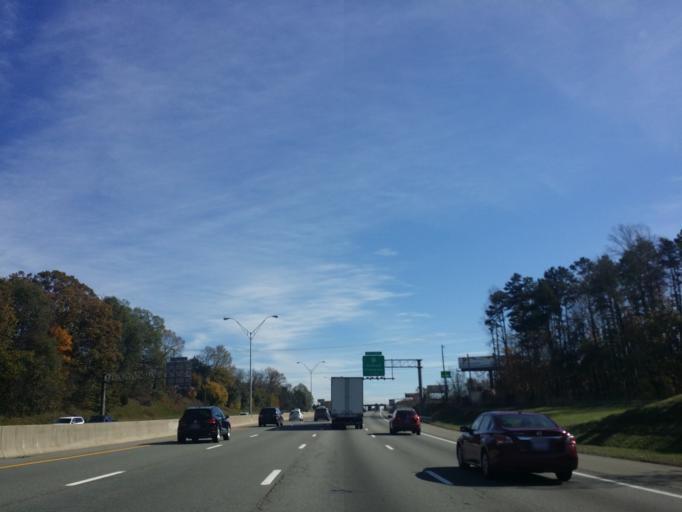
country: US
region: North Carolina
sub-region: Alamance County
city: Graham
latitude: 36.0623
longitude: -79.4146
